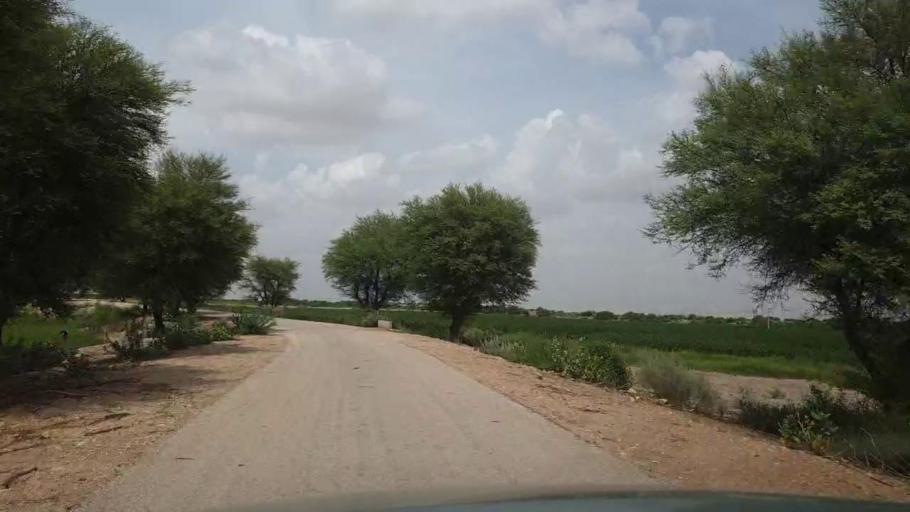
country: PK
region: Sindh
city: Kot Diji
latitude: 27.2279
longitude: 69.0889
